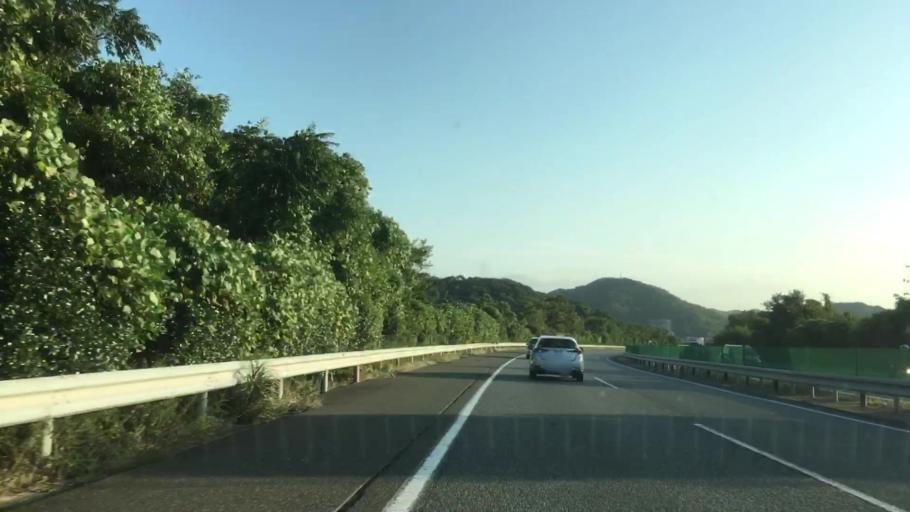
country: JP
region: Yamaguchi
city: Shimonoseki
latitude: 34.0178
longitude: 130.9577
